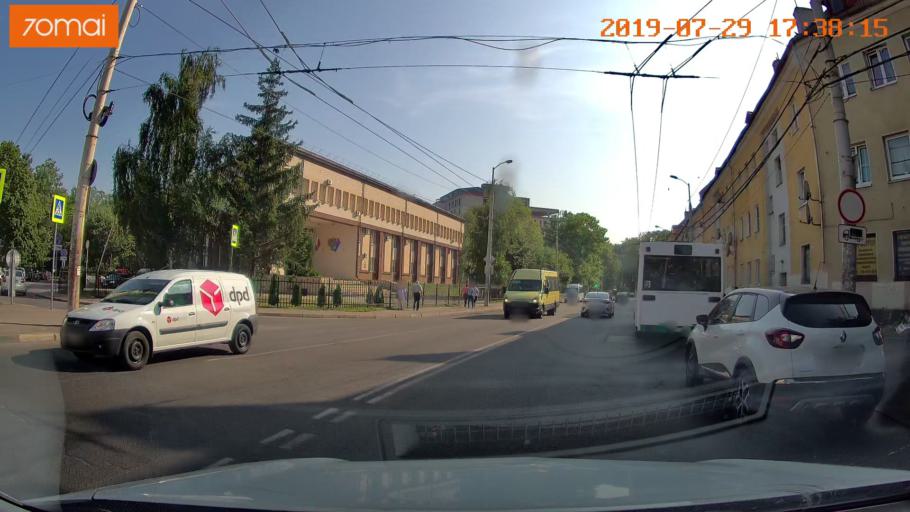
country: RU
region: Kaliningrad
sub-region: Gorod Kaliningrad
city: Kaliningrad
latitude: 54.7244
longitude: 20.5092
